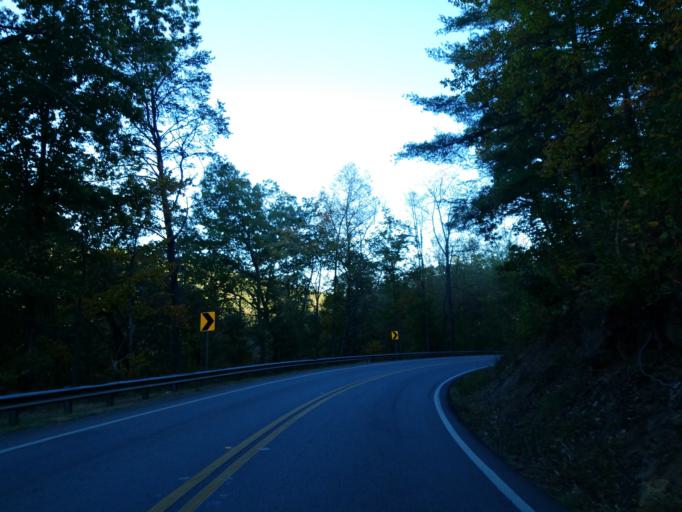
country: US
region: Georgia
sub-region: Dawson County
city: Dawsonville
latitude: 34.4288
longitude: -84.2192
